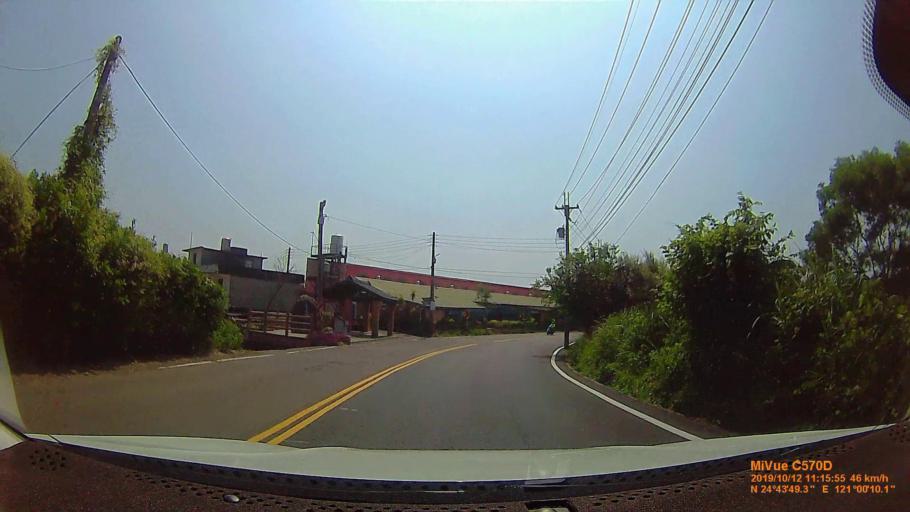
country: TW
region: Taiwan
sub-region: Hsinchu
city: Hsinchu
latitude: 24.7303
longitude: 121.0029
